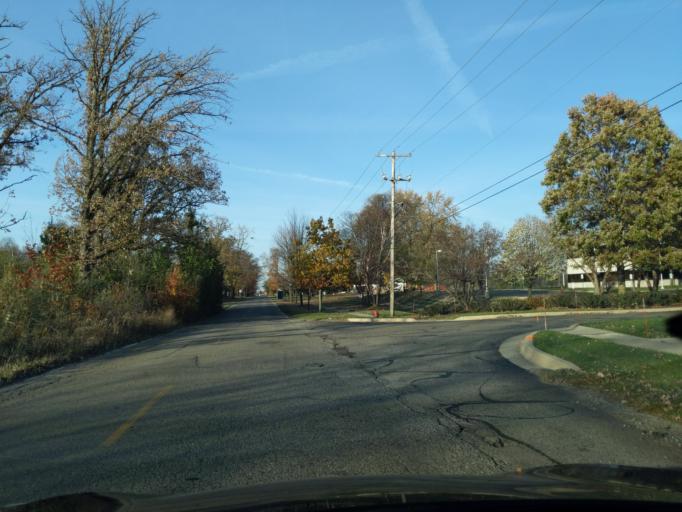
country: US
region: Michigan
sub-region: Ingham County
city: East Lansing
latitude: 42.7641
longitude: -84.5084
